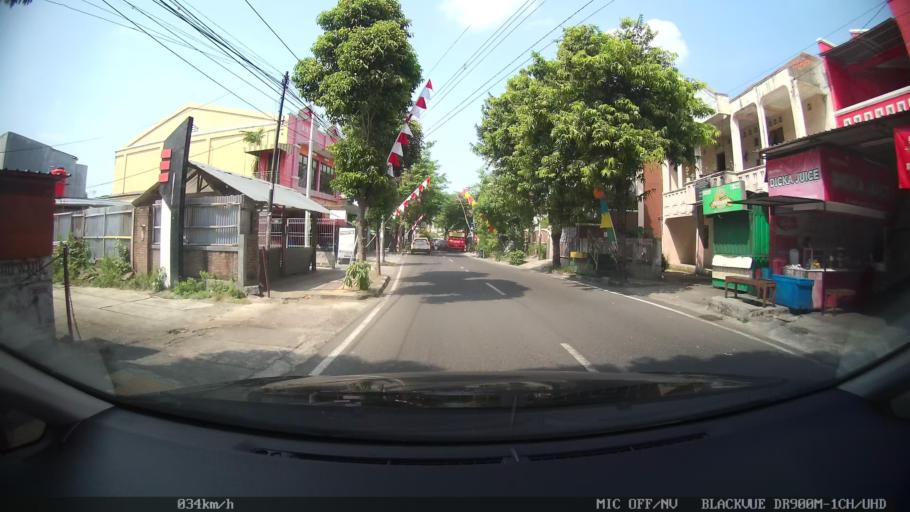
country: ID
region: Daerah Istimewa Yogyakarta
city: Yogyakarta
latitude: -7.8039
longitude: 110.3888
